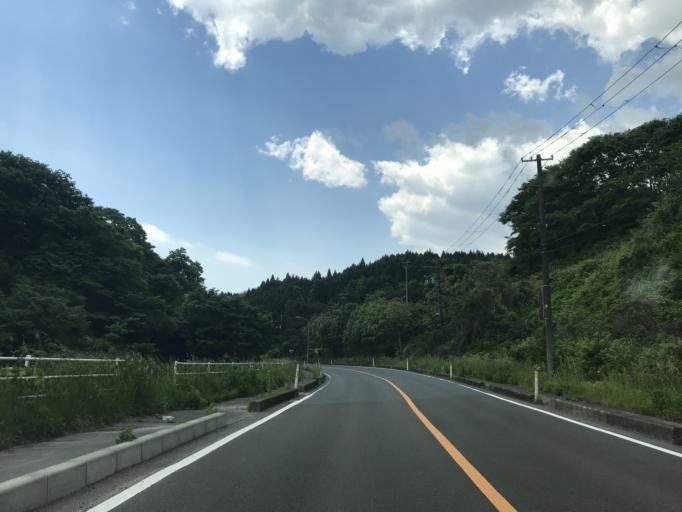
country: JP
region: Miyagi
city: Matsushima
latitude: 38.4107
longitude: 141.0636
